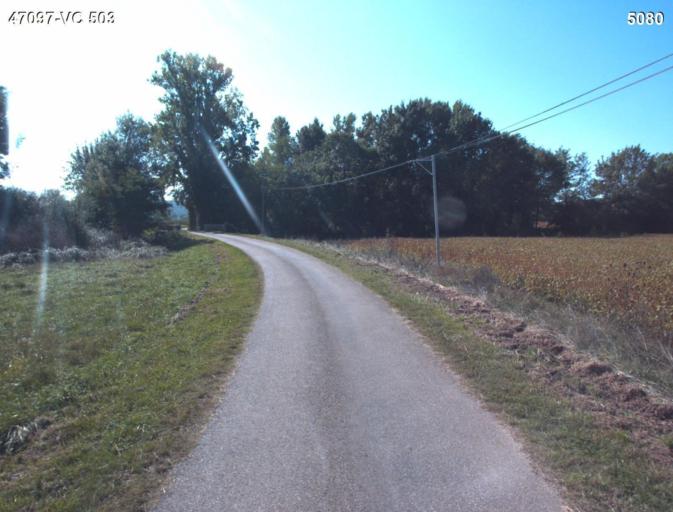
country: FR
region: Aquitaine
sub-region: Departement du Lot-et-Garonne
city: Port-Sainte-Marie
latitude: 44.2293
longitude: 0.3855
